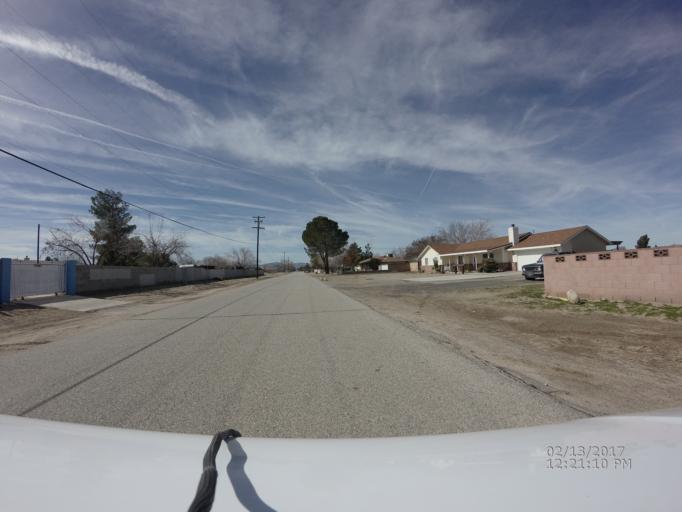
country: US
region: California
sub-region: Los Angeles County
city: Littlerock
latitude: 34.5653
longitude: -117.9308
